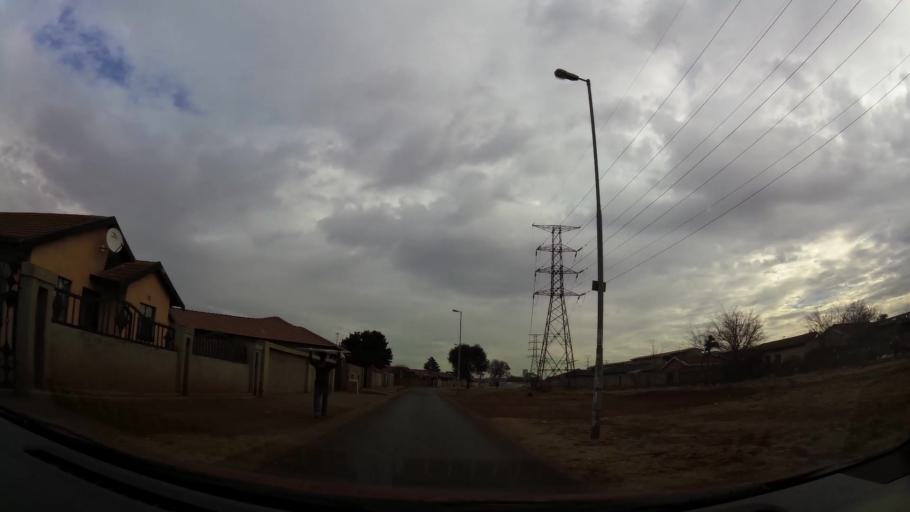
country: ZA
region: Gauteng
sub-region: City of Johannesburg Metropolitan Municipality
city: Soweto
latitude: -26.2807
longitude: 27.8447
